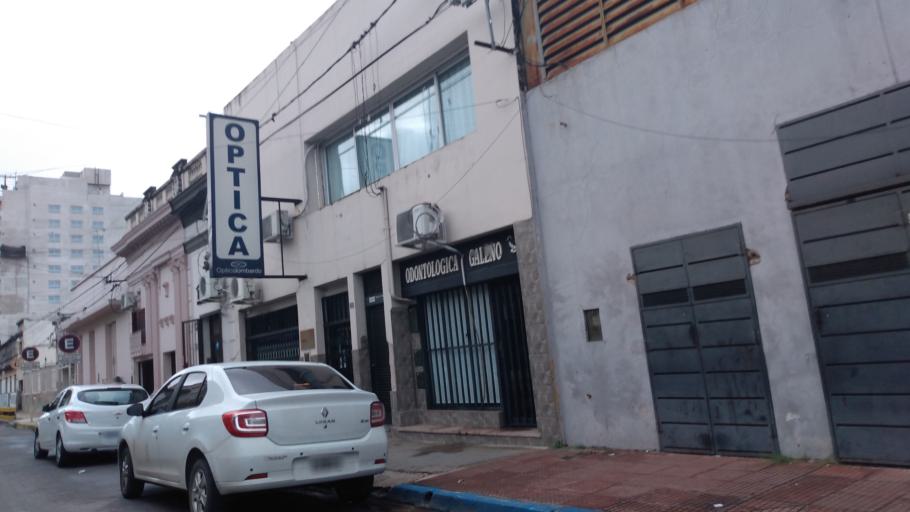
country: AR
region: Corrientes
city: Corrientes
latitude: -27.4698
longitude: -58.8333
